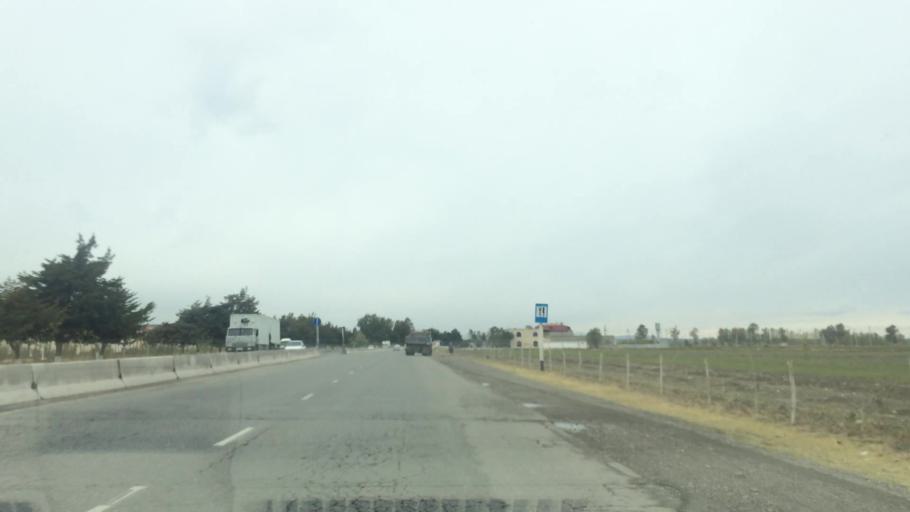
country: UZ
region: Samarqand
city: Bulung'ur
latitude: 39.7600
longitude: 67.2512
